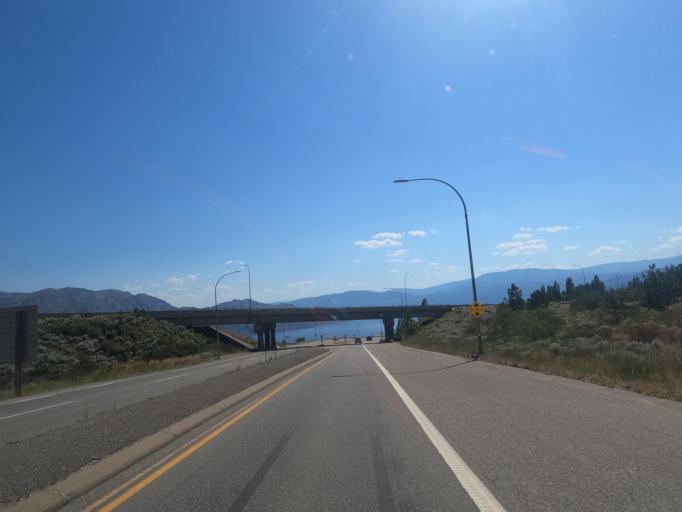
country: CA
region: British Columbia
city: Peachland
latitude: 49.8053
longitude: -119.6645
